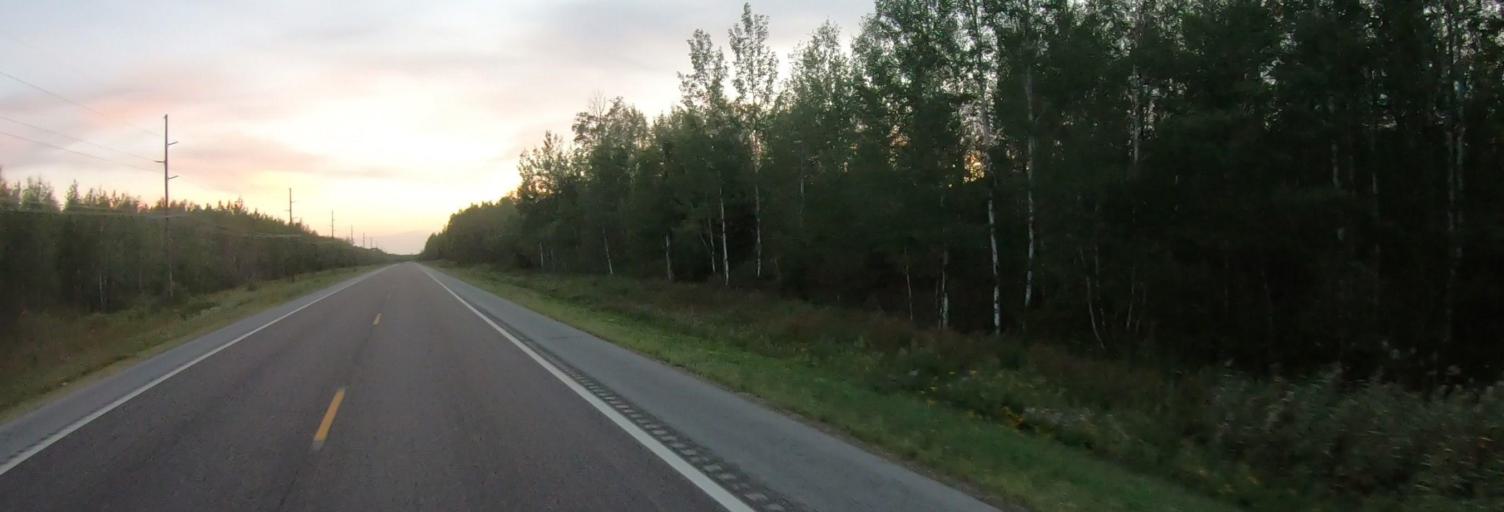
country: US
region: Minnesota
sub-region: Saint Louis County
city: Virginia
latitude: 47.8532
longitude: -92.4925
